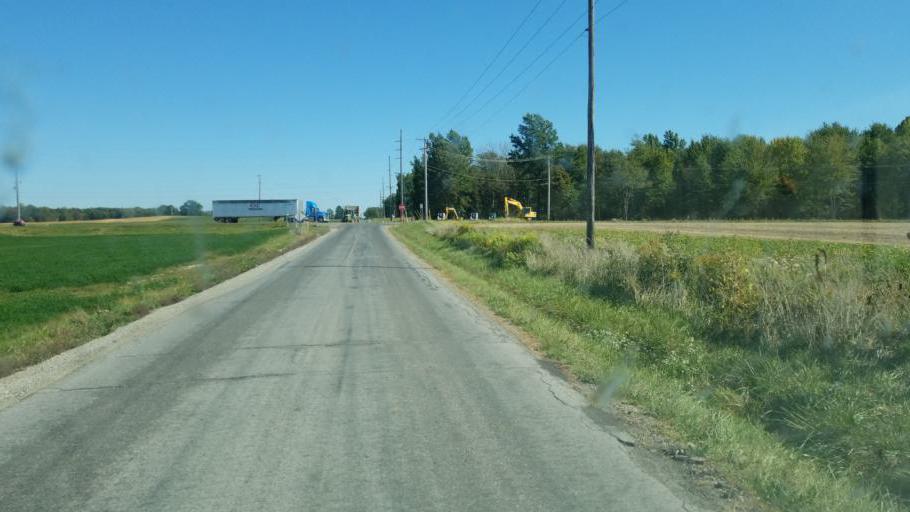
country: US
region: Ohio
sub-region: Huron County
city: Greenwich
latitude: 40.9930
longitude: -82.4883
